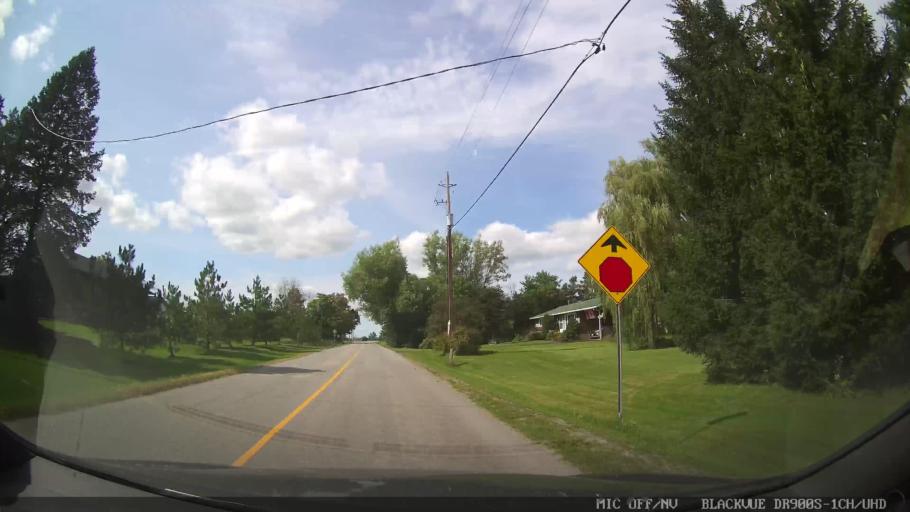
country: CA
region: Ontario
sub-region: Lanark County
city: Smiths Falls
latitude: 44.8883
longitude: -75.9270
